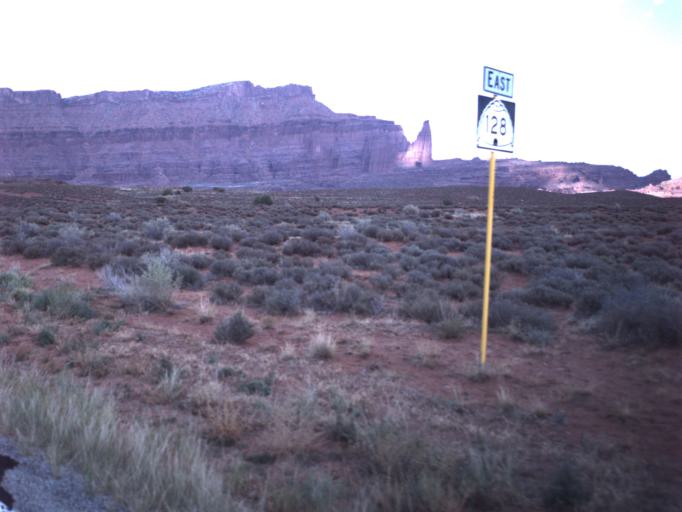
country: US
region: Utah
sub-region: Grand County
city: Moab
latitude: 38.7224
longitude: -109.3586
